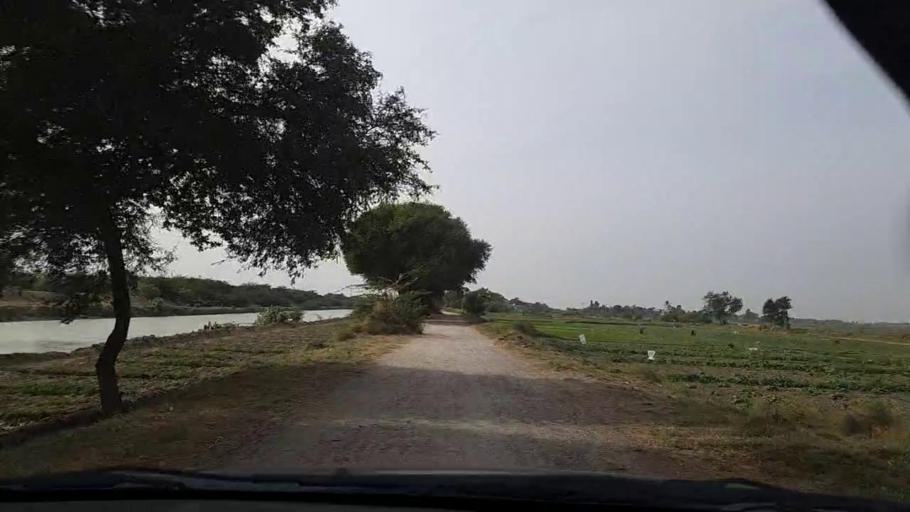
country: PK
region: Sindh
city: Thatta
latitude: 24.5688
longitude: 67.8667
